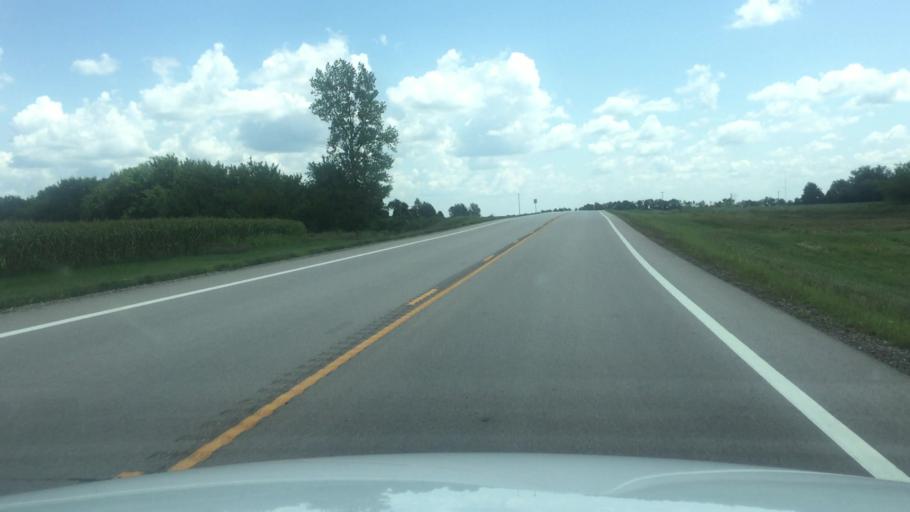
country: US
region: Kansas
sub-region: Brown County
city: Horton
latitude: 39.6662
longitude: -95.4190
